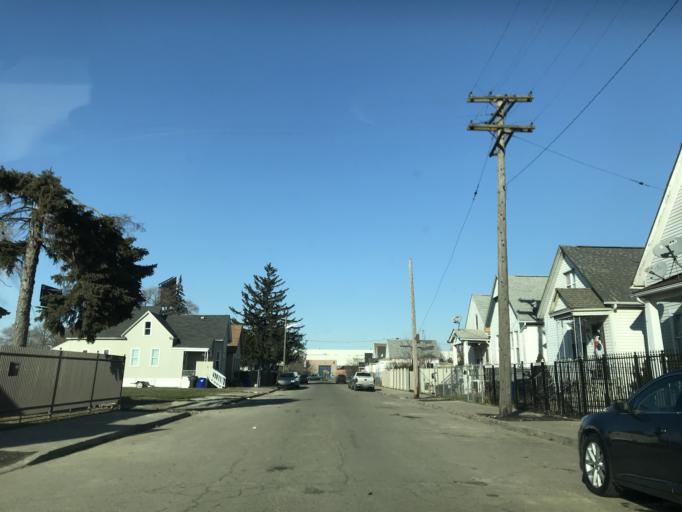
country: US
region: Michigan
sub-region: Wayne County
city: Dearborn
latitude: 42.3372
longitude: -83.1199
